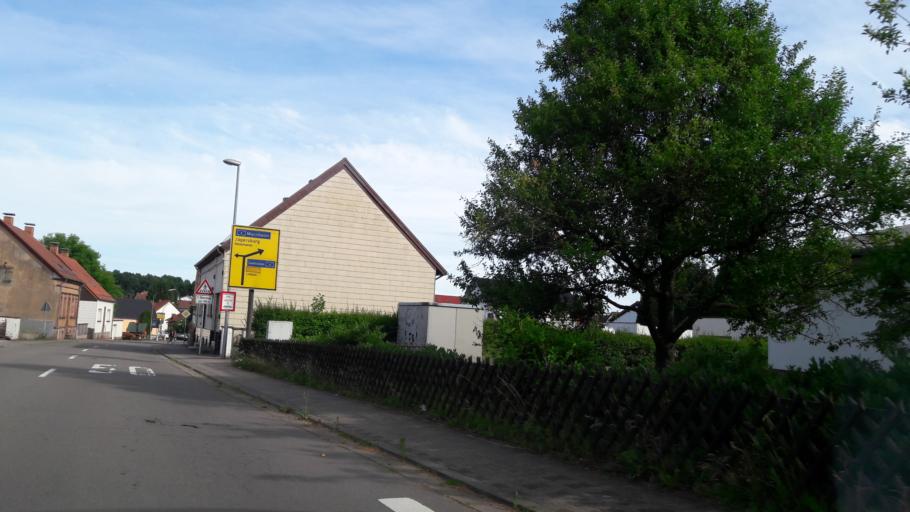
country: DE
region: Saarland
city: Bexbach
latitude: 49.3252
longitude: 7.2859
